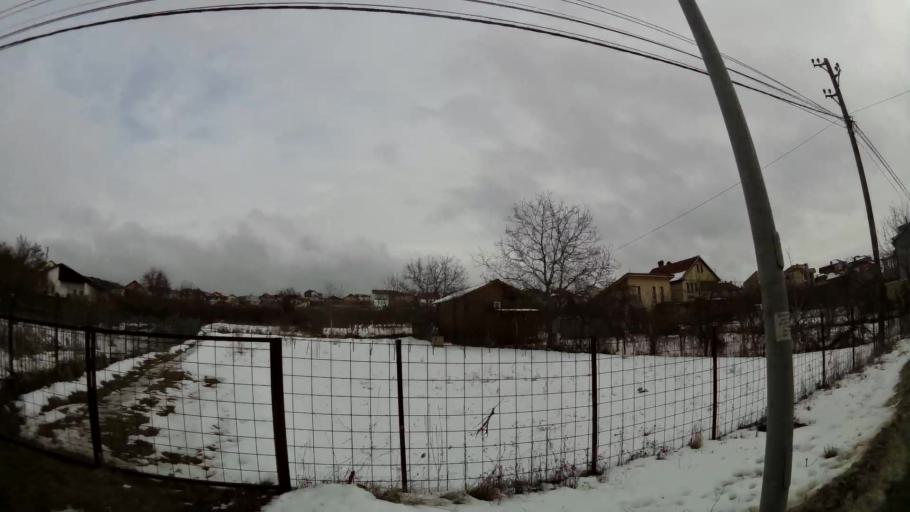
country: XK
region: Pristina
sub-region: Komuna e Prishtines
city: Pristina
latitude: 42.6512
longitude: 21.1935
